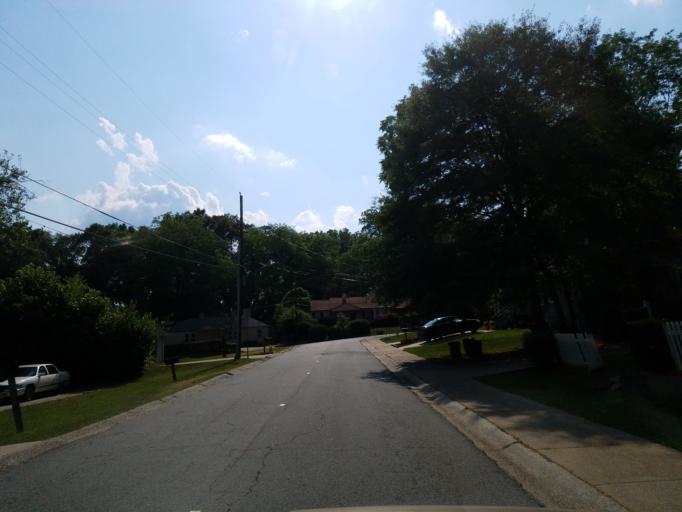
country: US
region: Georgia
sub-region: Cobb County
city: Marietta
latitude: 33.9578
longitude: -84.5413
